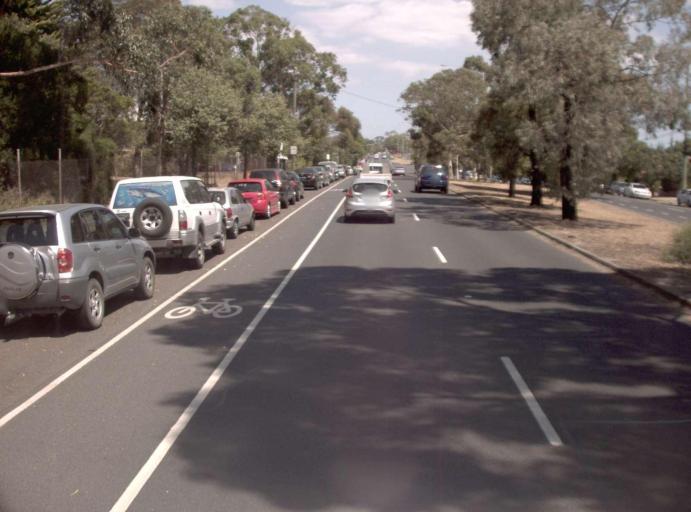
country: AU
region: Victoria
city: McKinnon
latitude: -37.9175
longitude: 145.0599
